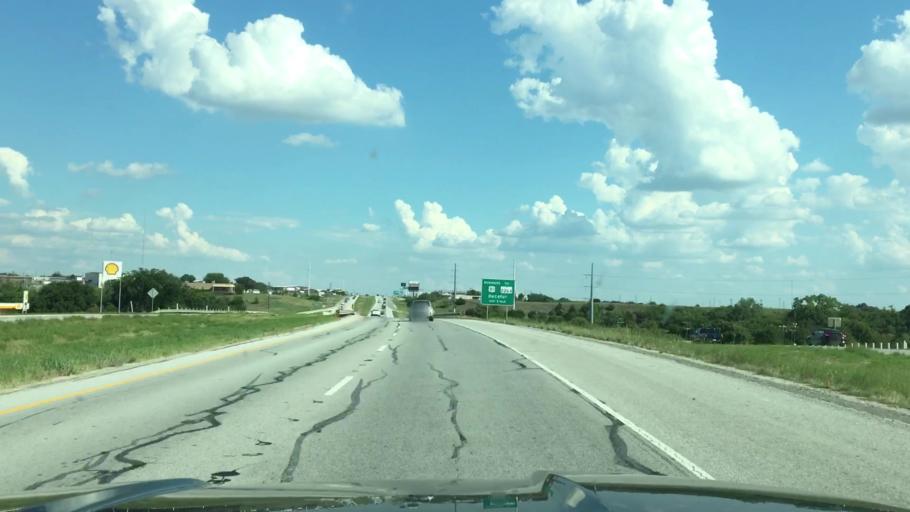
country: US
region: Texas
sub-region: Wise County
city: Decatur
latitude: 33.2155
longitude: -97.5853
